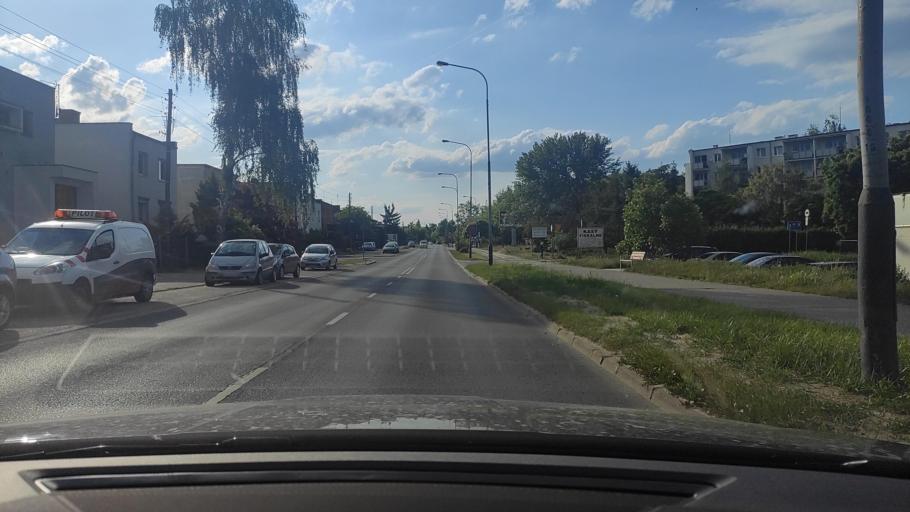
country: PL
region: Greater Poland Voivodeship
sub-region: Poznan
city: Poznan
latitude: 52.4498
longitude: 16.9390
